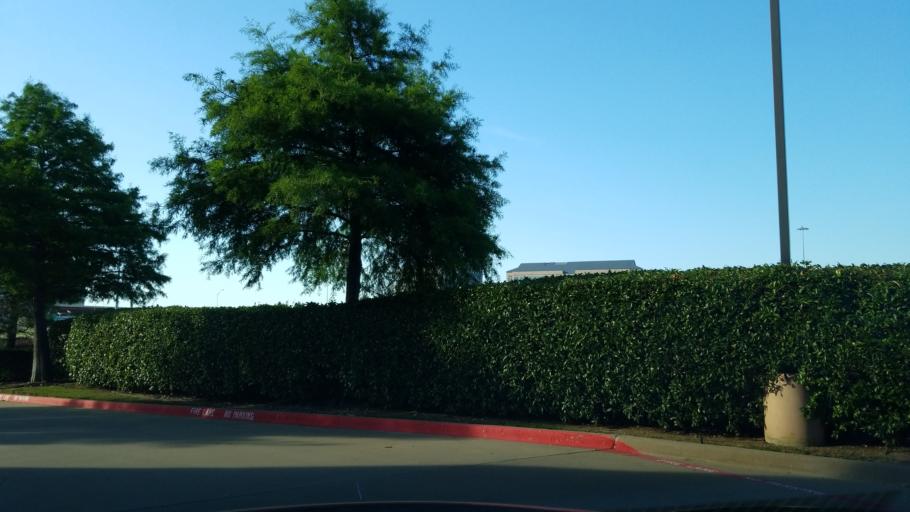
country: US
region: Texas
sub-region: Dallas County
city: Coppell
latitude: 32.8915
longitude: -96.9703
